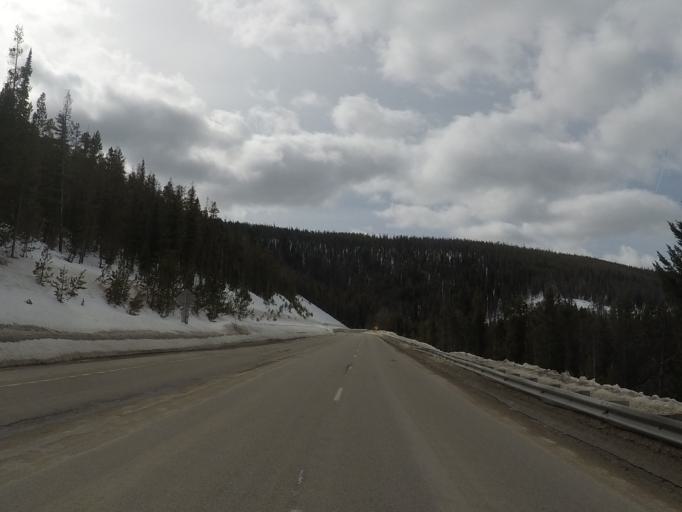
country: US
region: Idaho
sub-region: Lemhi County
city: Salmon
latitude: 45.7092
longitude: -113.9346
